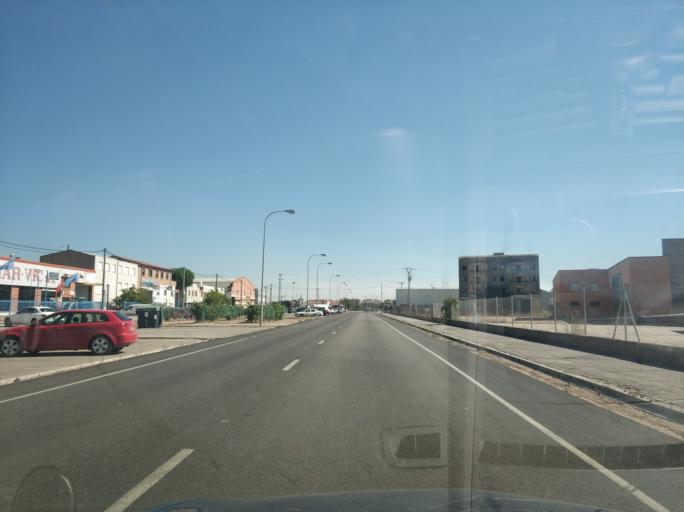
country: ES
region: Castille and Leon
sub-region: Provincia de Burgos
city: Aranda de Duero
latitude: 41.6672
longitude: -3.7052
